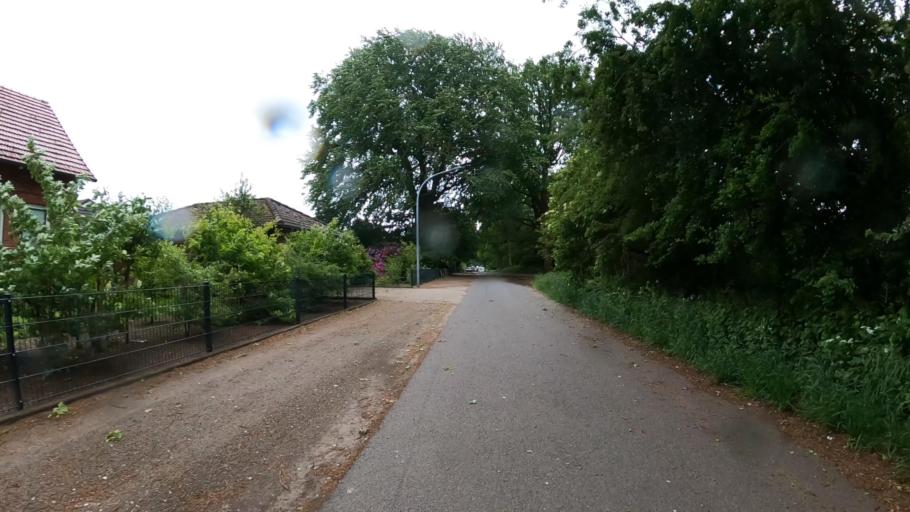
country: DE
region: Hamburg
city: Langenhorn
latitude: 53.6964
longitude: 10.0205
